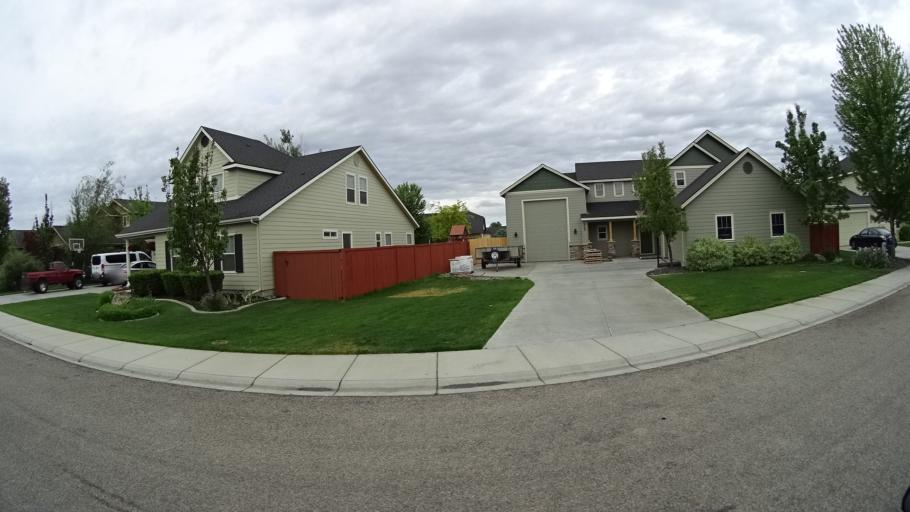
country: US
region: Idaho
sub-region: Ada County
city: Star
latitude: 43.7005
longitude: -116.4787
